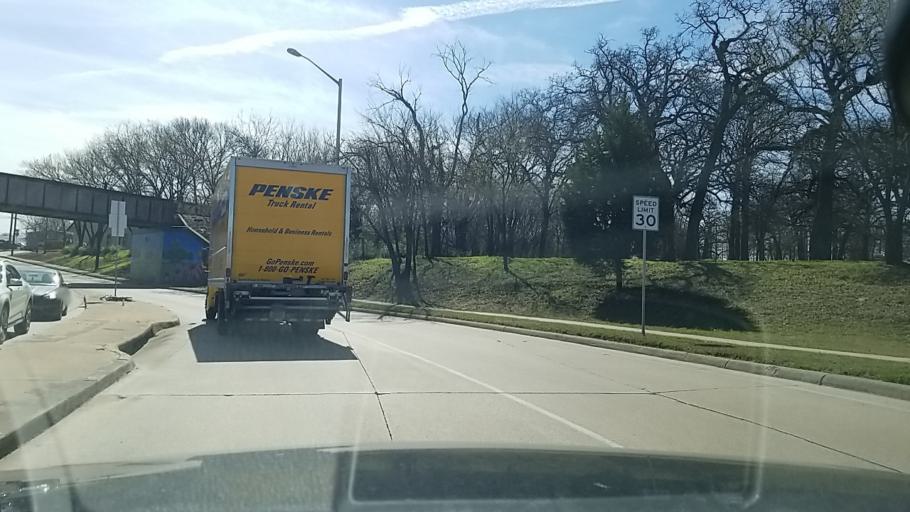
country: US
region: Texas
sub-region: Denton County
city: Denton
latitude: 33.2061
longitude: -97.1319
